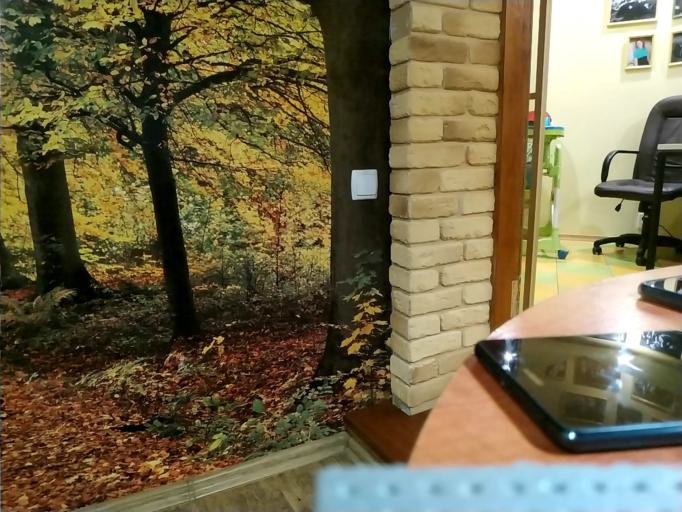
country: RU
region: Tverskaya
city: Zubtsov
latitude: 56.2075
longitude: 34.7150
